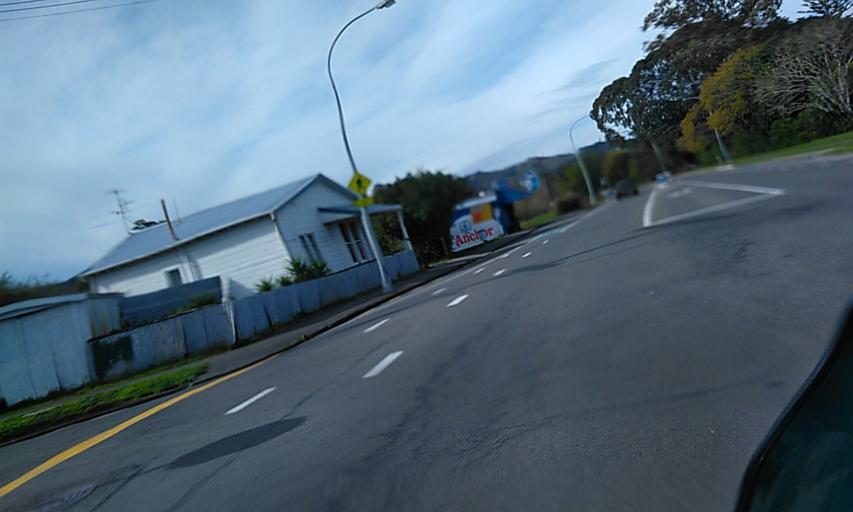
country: NZ
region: Gisborne
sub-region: Gisborne District
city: Gisborne
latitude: -38.6559
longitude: 178.0186
